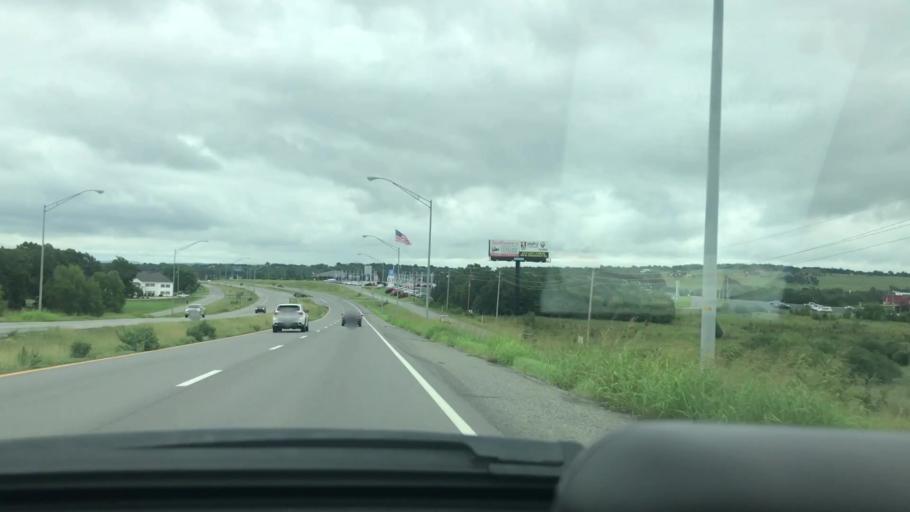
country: US
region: Oklahoma
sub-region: Pittsburg County
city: McAlester
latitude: 34.8984
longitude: -95.7576
